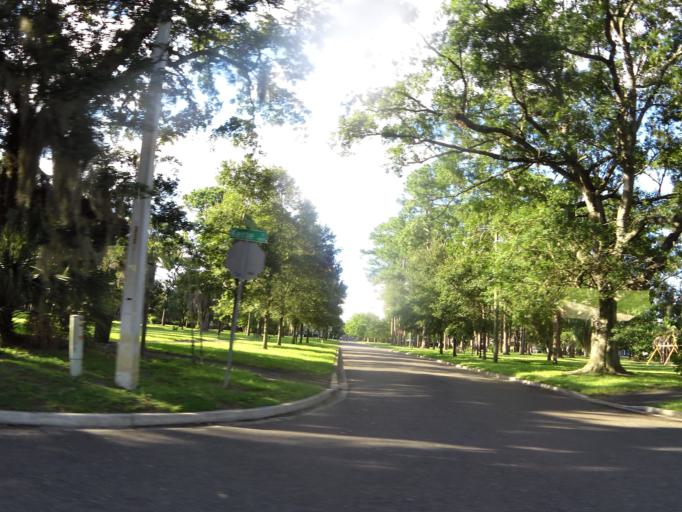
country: US
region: Florida
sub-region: Duval County
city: Jacksonville
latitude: 30.3114
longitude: -81.7245
